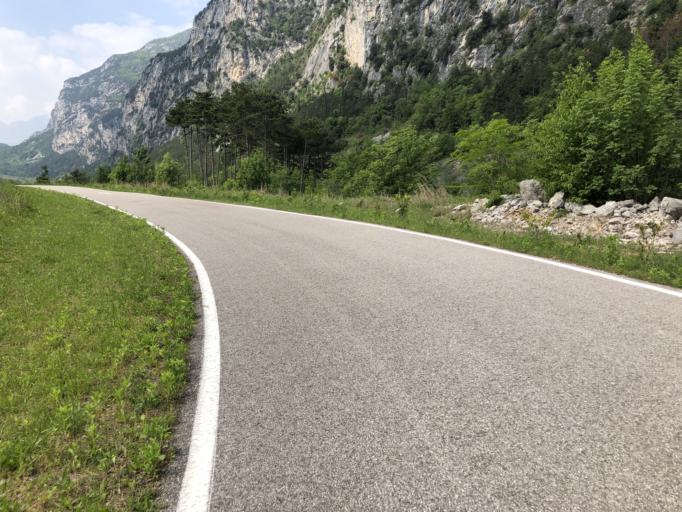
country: IT
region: Trentino-Alto Adige
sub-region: Provincia di Trento
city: Dro
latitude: 45.9701
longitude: 10.9133
